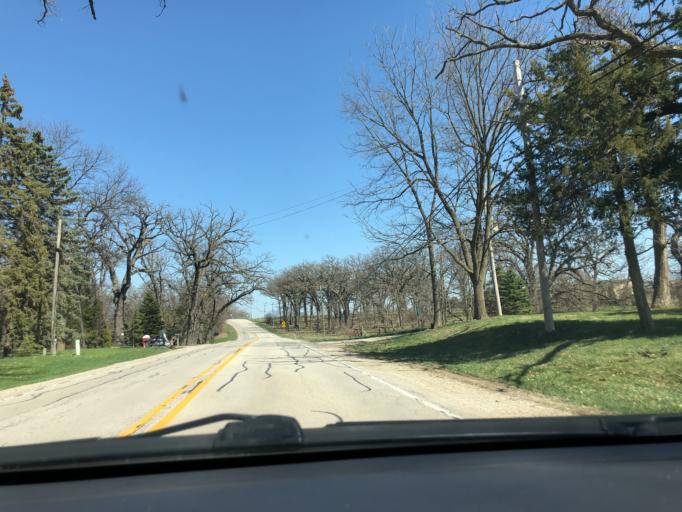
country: US
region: Illinois
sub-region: McHenry County
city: Huntley
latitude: 42.1662
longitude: -88.4698
